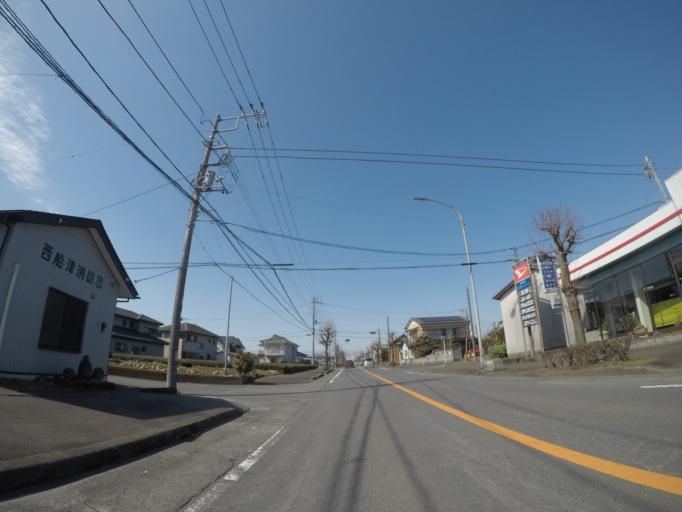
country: JP
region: Shizuoka
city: Fuji
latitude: 35.1508
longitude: 138.7637
